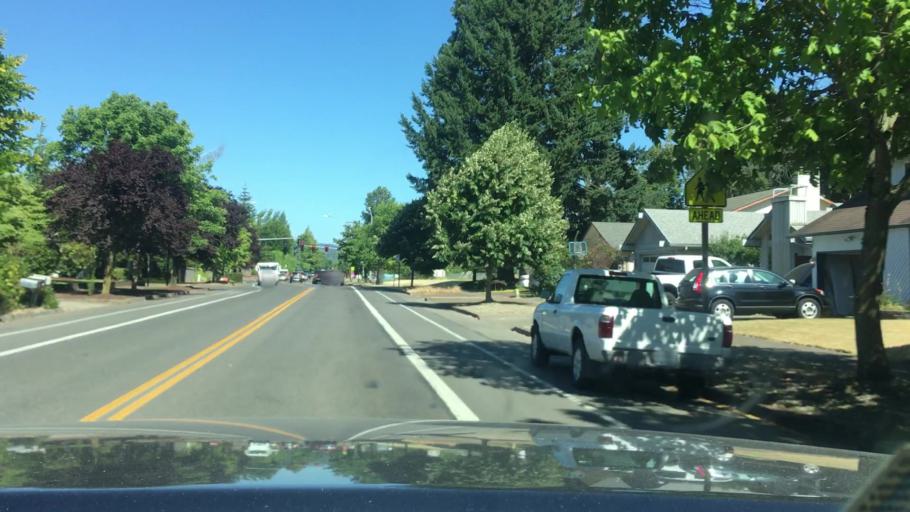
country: US
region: Oregon
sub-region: Lane County
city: Eugene
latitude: 44.0929
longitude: -123.0828
